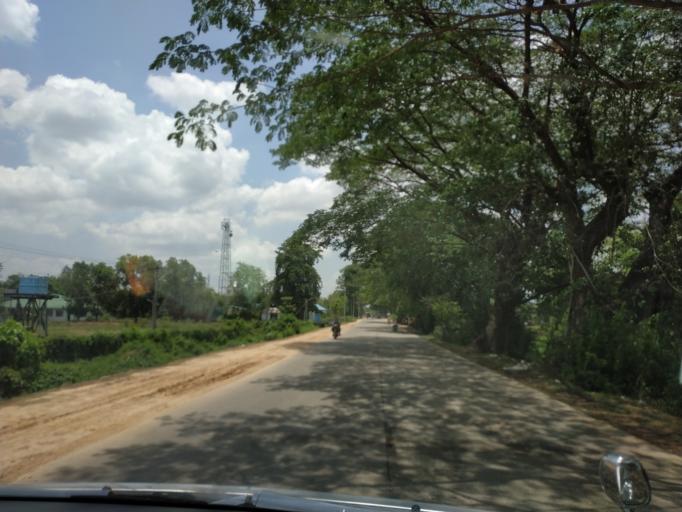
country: MM
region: Bago
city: Bago
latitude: 17.4763
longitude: 96.5131
